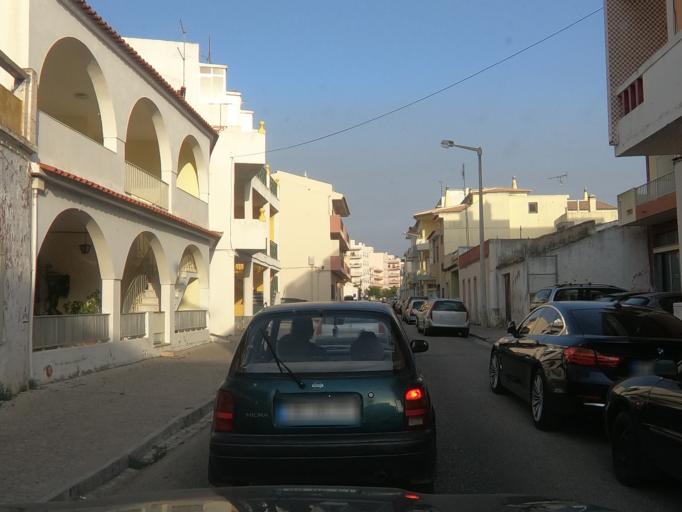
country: PT
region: Faro
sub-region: Loule
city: Loule
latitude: 37.1340
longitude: -8.0108
